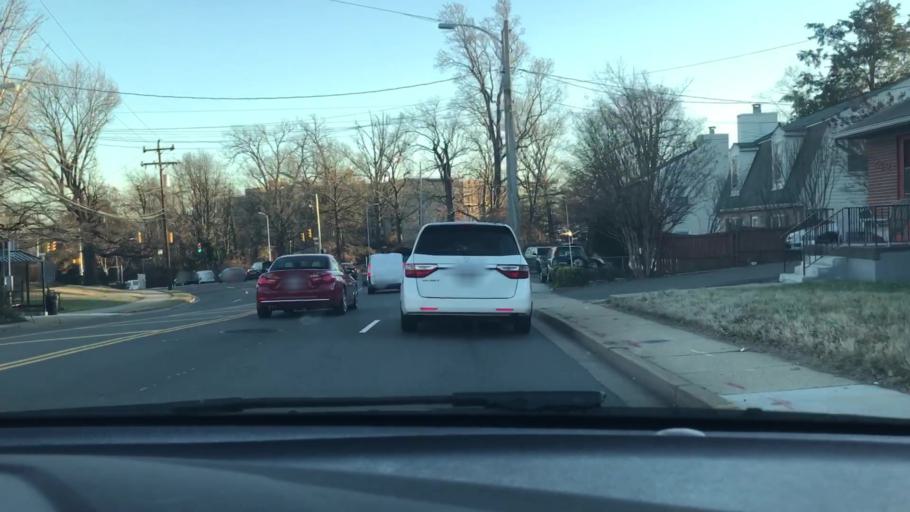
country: US
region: Virginia
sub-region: Fairfax County
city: Baileys Crossroads
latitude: 38.8612
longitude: -77.1291
